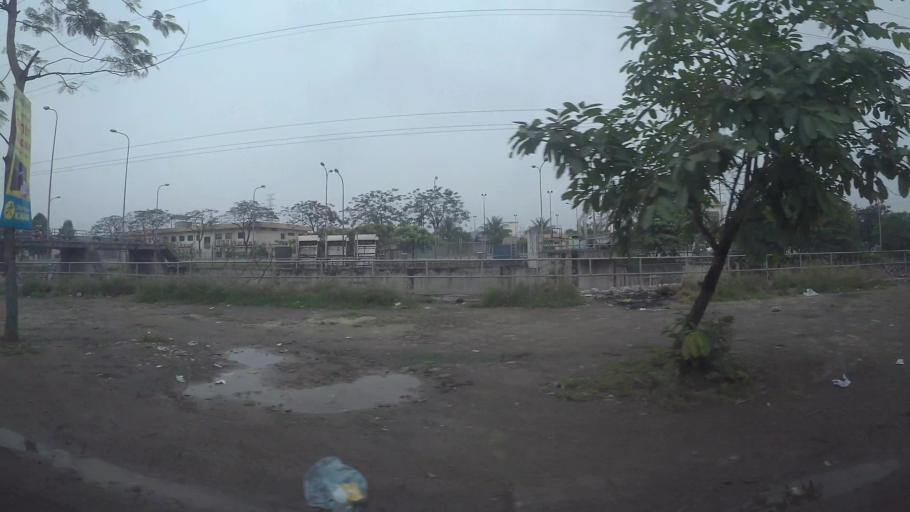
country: VN
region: Ha Noi
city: Van Dien
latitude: 20.9781
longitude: 105.8651
